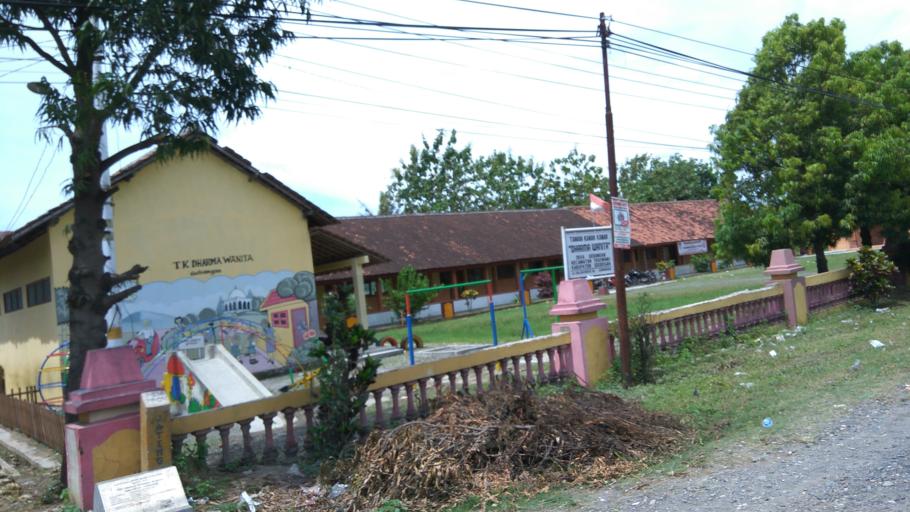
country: ID
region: Central Java
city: Mranggen
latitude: -7.0507
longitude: 110.6279
